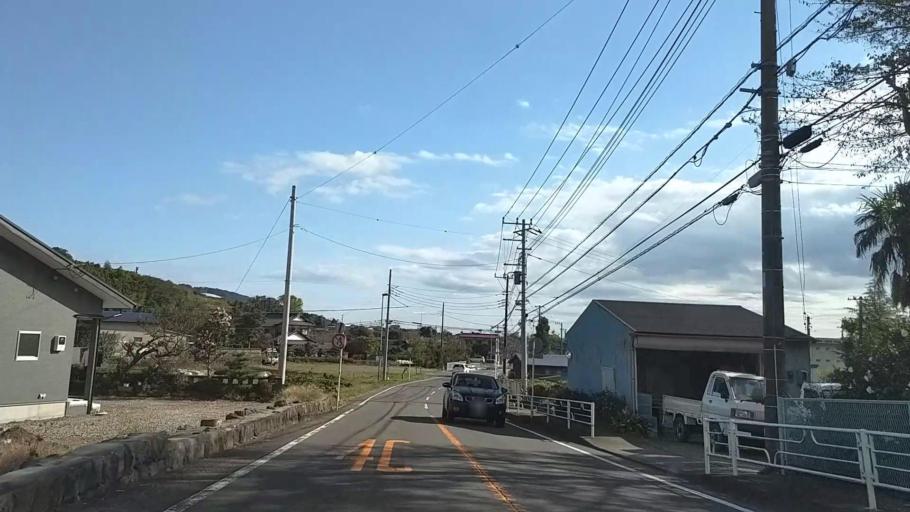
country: JP
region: Kanagawa
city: Odawara
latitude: 35.3141
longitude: 139.1751
